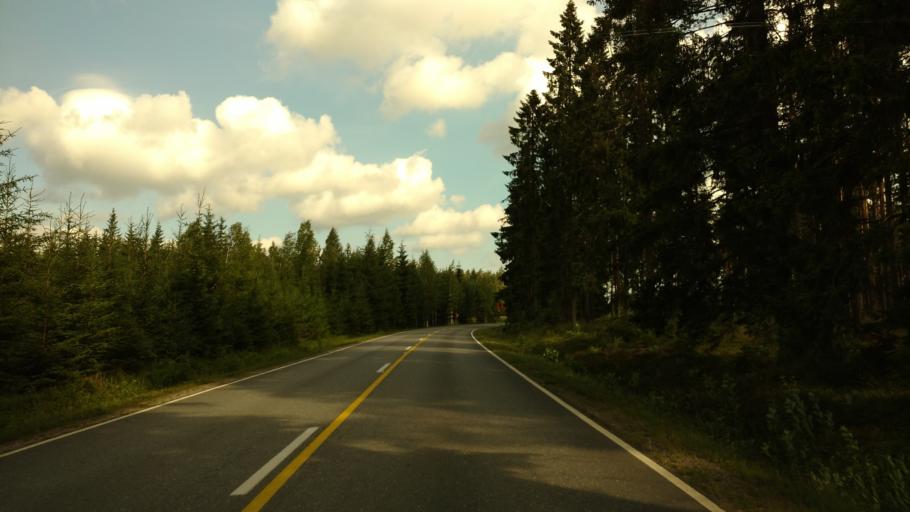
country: FI
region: Varsinais-Suomi
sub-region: Loimaa
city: Koski Tl
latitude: 60.6208
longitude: 23.1131
